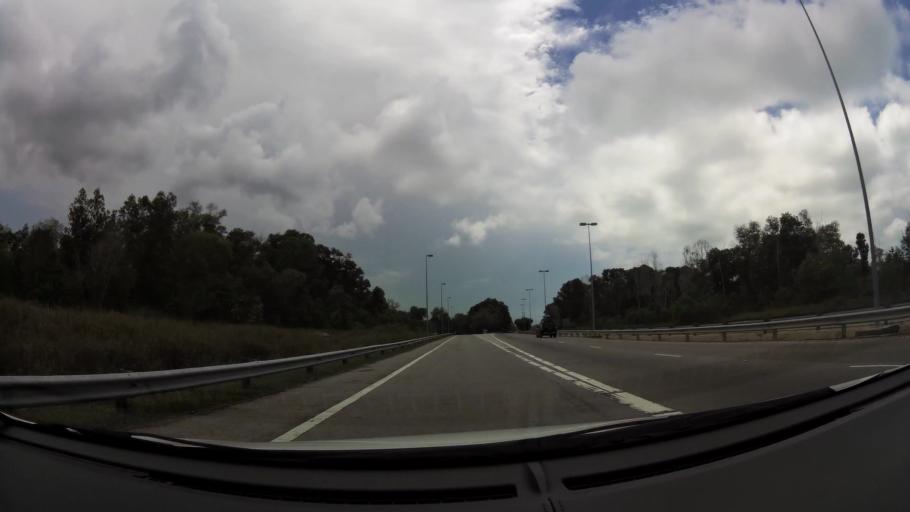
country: BN
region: Brunei and Muara
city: Bandar Seri Begawan
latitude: 4.9759
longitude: 114.8849
